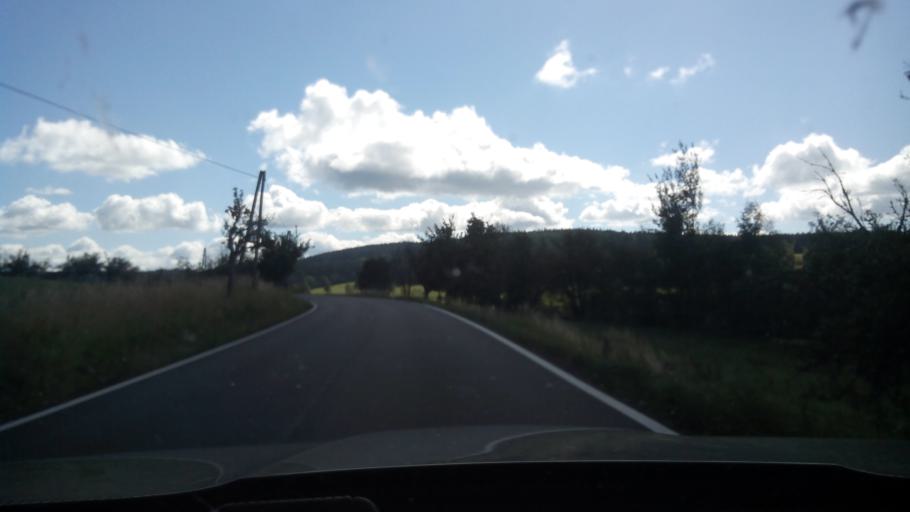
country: CZ
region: Jihocesky
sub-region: Okres Prachatice
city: Stachy
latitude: 49.1266
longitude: 13.6131
